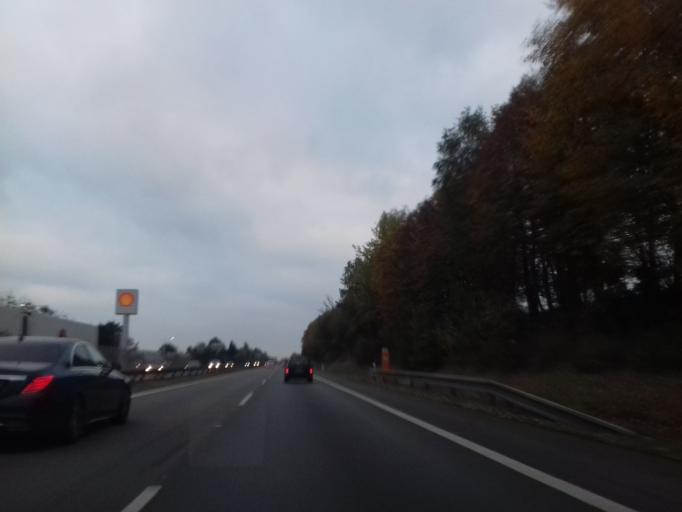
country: CZ
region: Central Bohemia
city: Zruc nad Sazavou
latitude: 49.7124
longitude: 15.0643
